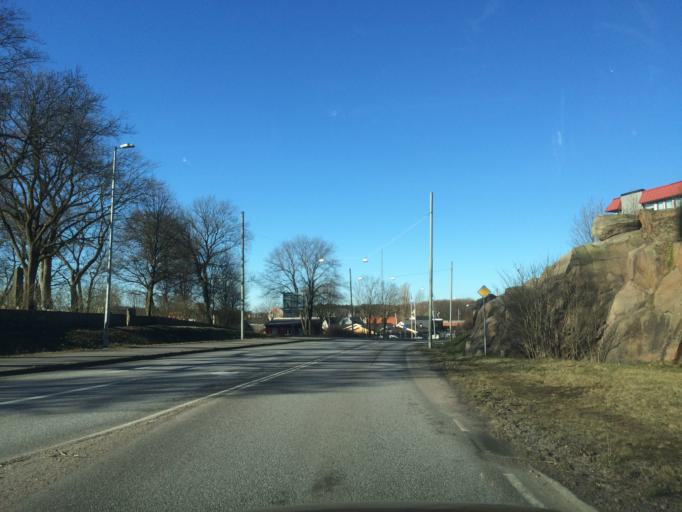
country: SE
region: Vaestra Goetaland
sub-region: Goteborg
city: Majorna
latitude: 57.6486
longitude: 11.9390
